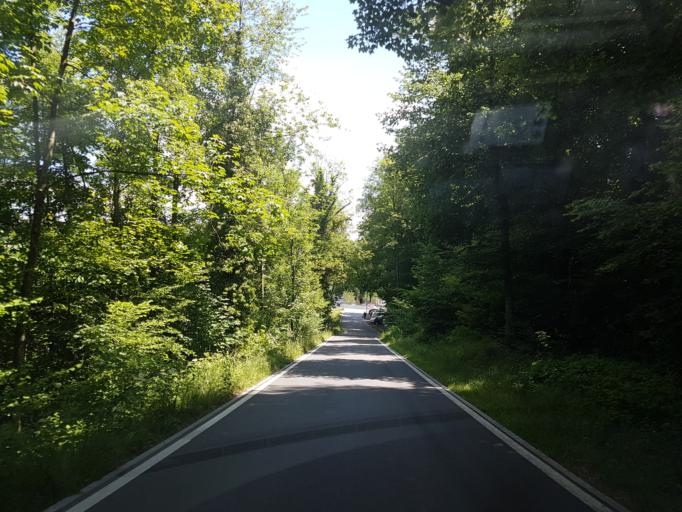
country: CH
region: Aargau
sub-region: Bezirk Baden
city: Niederrohrdorf
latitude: 47.3937
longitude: 8.2997
